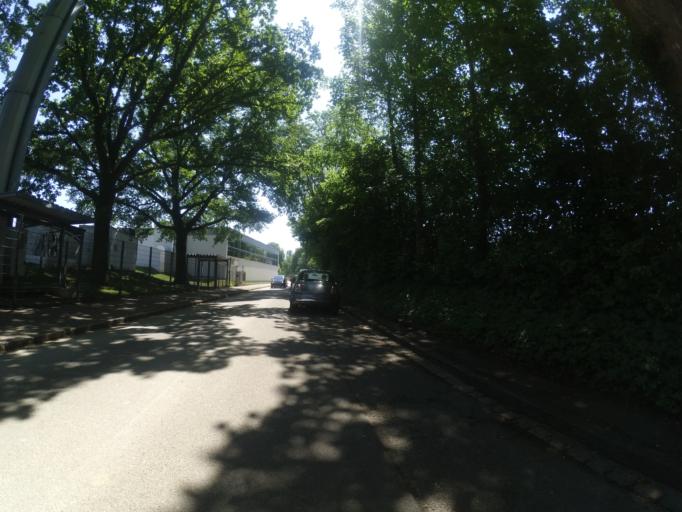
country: DE
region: Bavaria
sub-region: Swabia
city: Neu-Ulm
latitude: 48.4036
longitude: 10.0094
